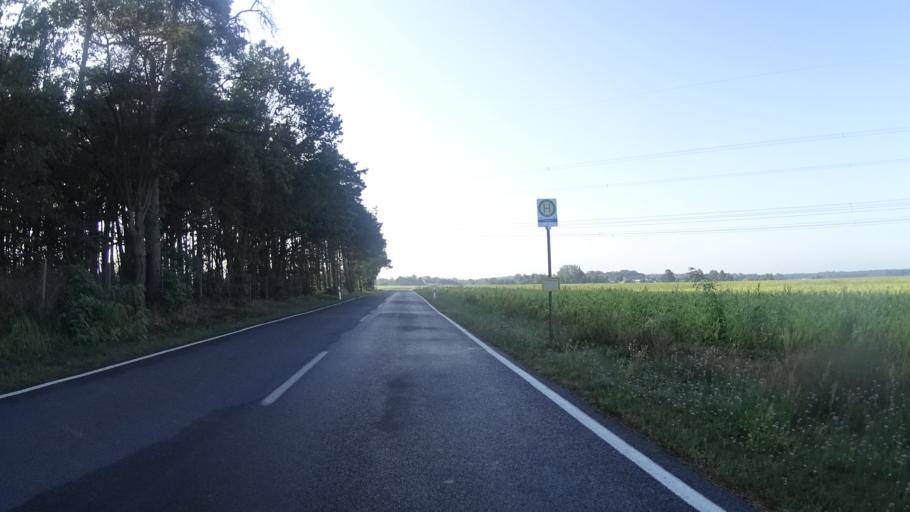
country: DE
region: Brandenburg
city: Kasel-Golzig
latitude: 51.9977
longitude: 13.6902
